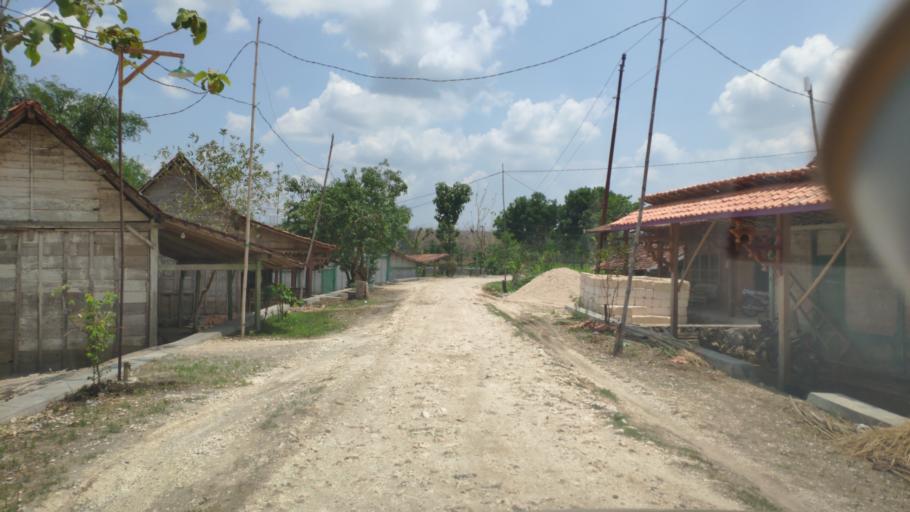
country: ID
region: Central Java
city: Bacem
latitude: -7.0572
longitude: 111.3732
